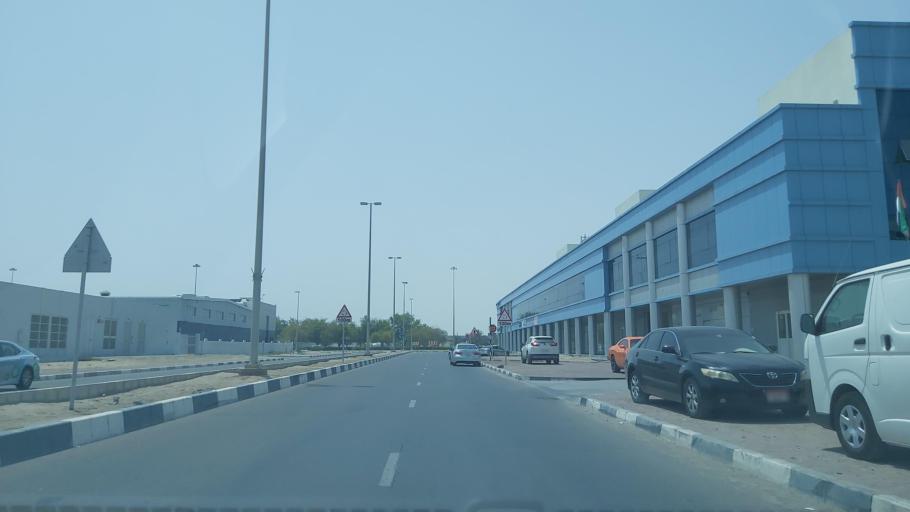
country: AE
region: Abu Dhabi
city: Abu Dhabi
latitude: 24.3760
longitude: 54.5202
